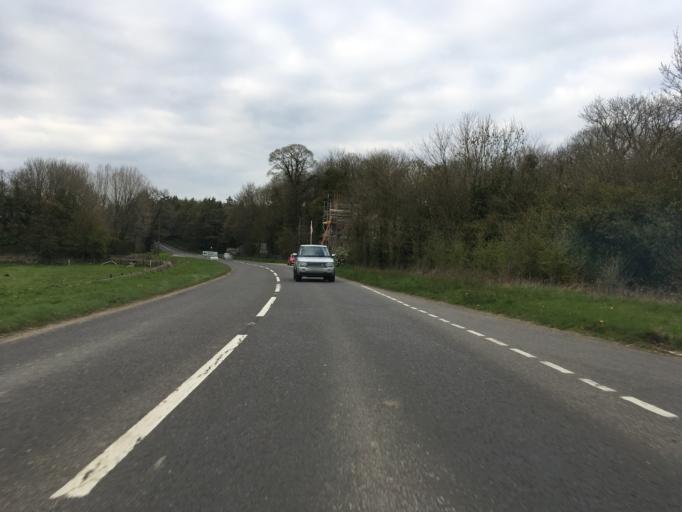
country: GB
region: England
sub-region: Gloucestershire
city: Coates
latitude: 51.6874
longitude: -2.0047
